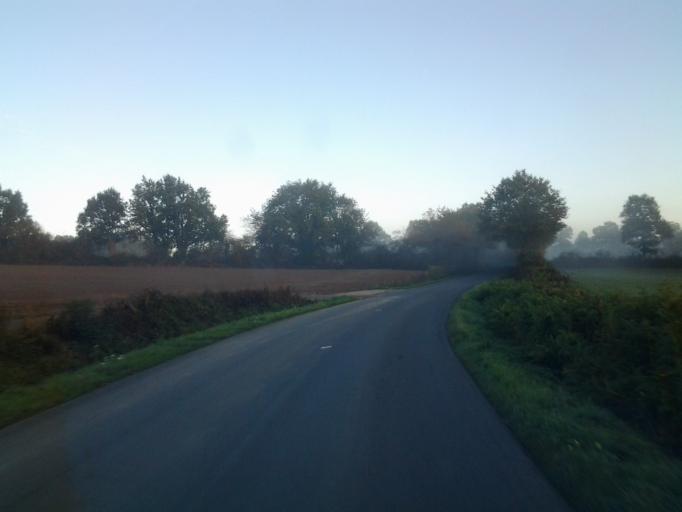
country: FR
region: Pays de la Loire
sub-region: Departement de la Vendee
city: Chateau-Guibert
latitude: 46.6301
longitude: -1.2331
